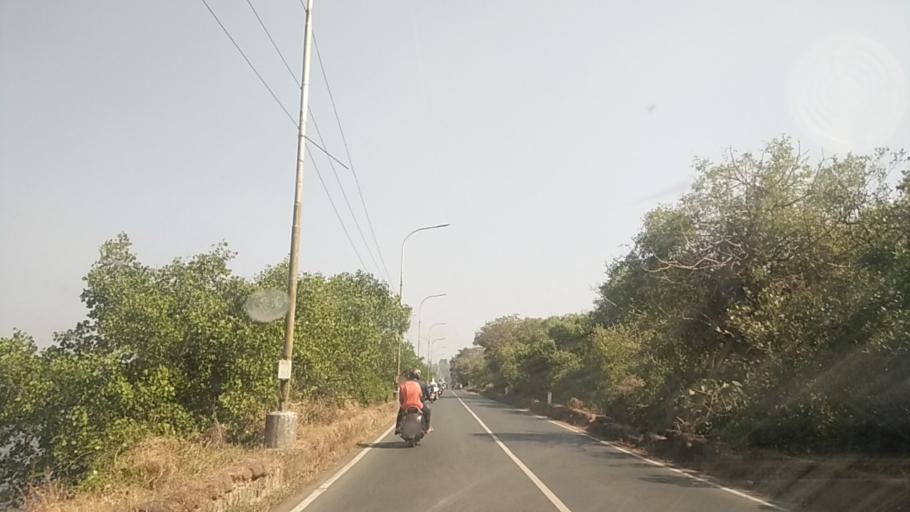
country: IN
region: Goa
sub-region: North Goa
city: Panaji
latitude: 15.5022
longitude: 73.8521
